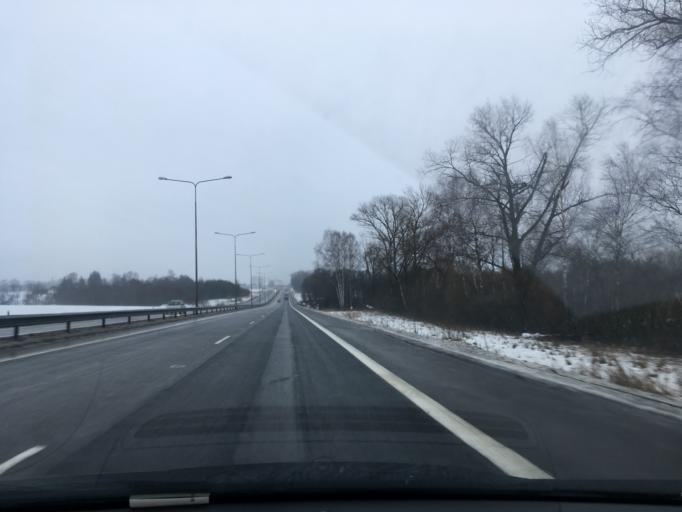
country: LT
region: Vilnius County
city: Elektrenai
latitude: 54.7929
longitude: 24.6255
